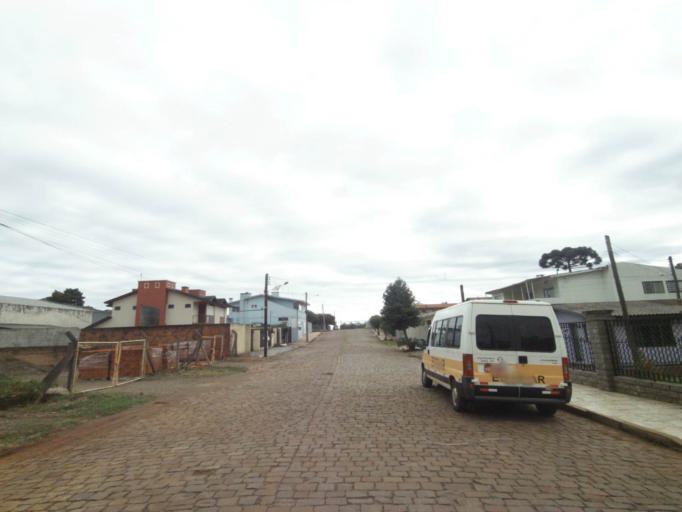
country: BR
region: Rio Grande do Sul
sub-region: Lagoa Vermelha
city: Lagoa Vermelha
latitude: -28.2163
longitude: -51.5166
